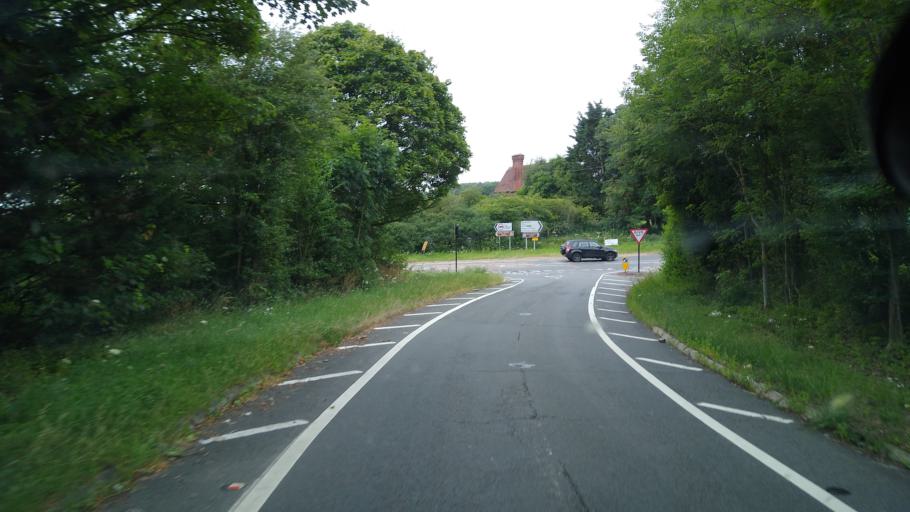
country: GB
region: England
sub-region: Hampshire
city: Alton
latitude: 51.1361
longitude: -0.9763
